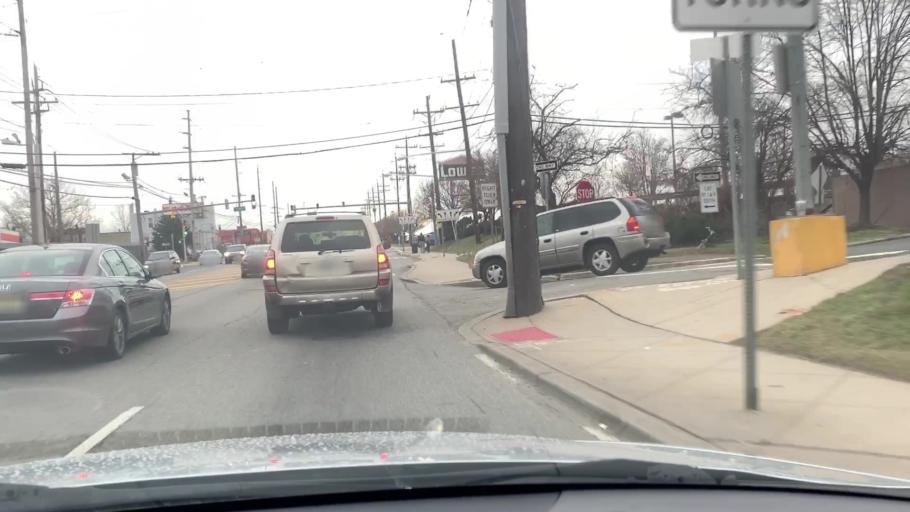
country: US
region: New Jersey
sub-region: Hudson County
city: North Bergen
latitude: 40.8069
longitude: -74.0167
